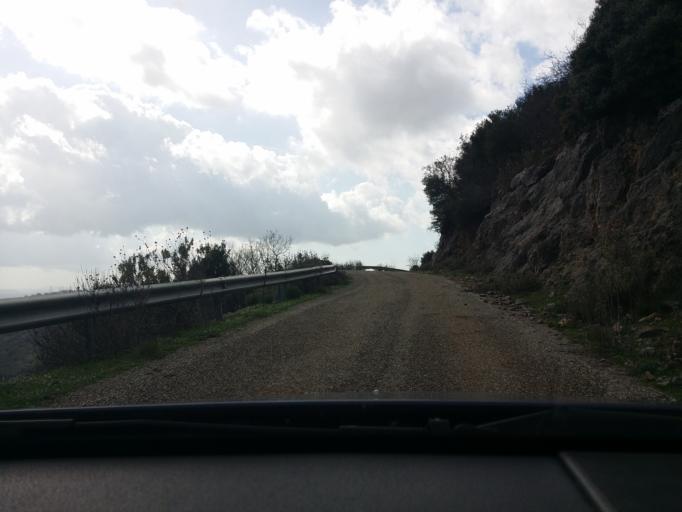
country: GR
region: West Greece
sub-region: Nomos Aitolias kai Akarnanias
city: Fitiai
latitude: 38.6470
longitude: 21.1980
